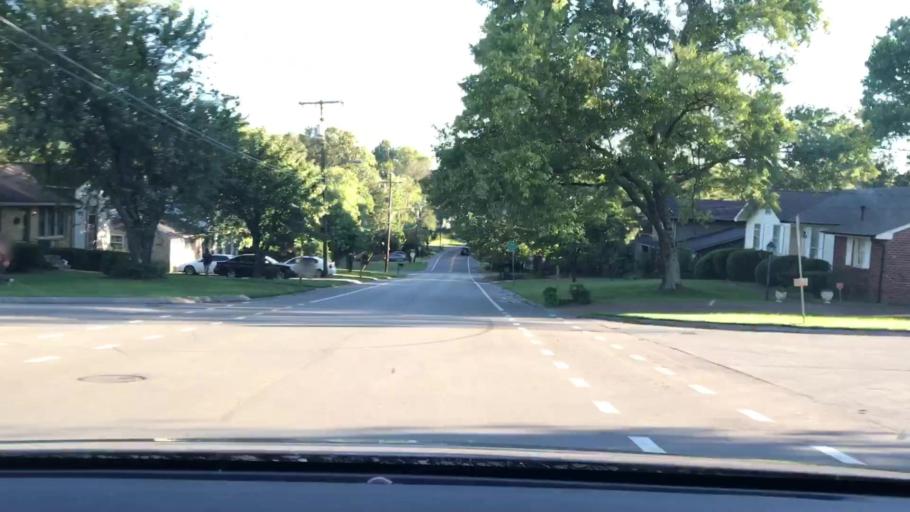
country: US
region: Tennessee
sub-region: Williamson County
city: Brentwood Estates
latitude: 36.0525
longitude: -86.7027
